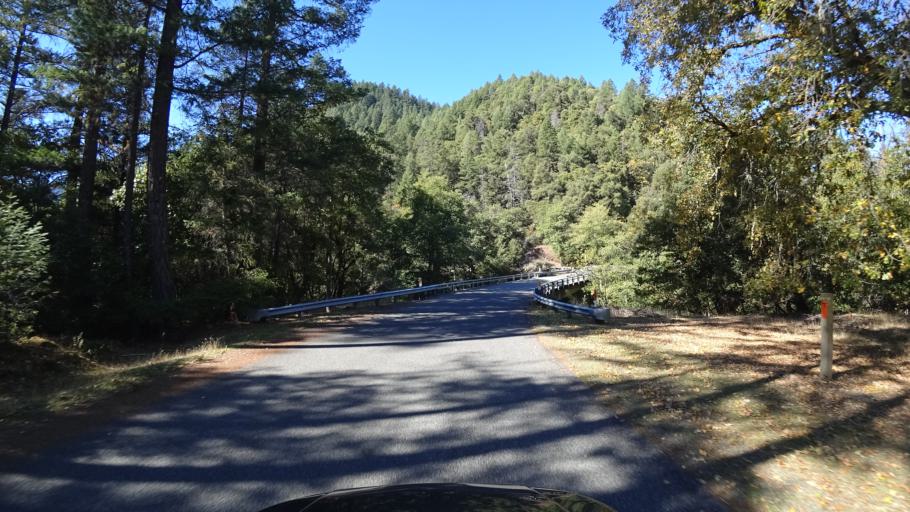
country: US
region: California
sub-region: Humboldt County
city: Willow Creek
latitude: 41.2414
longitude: -123.2923
